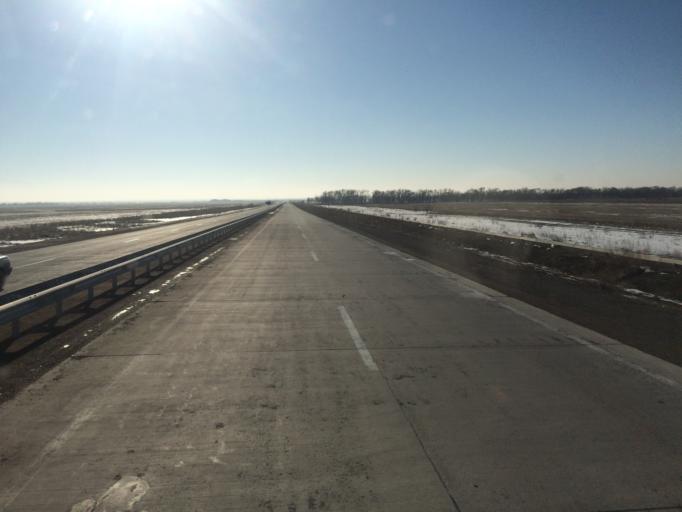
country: KG
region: Chuy
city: Sokuluk
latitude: 43.3010
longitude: 74.2523
